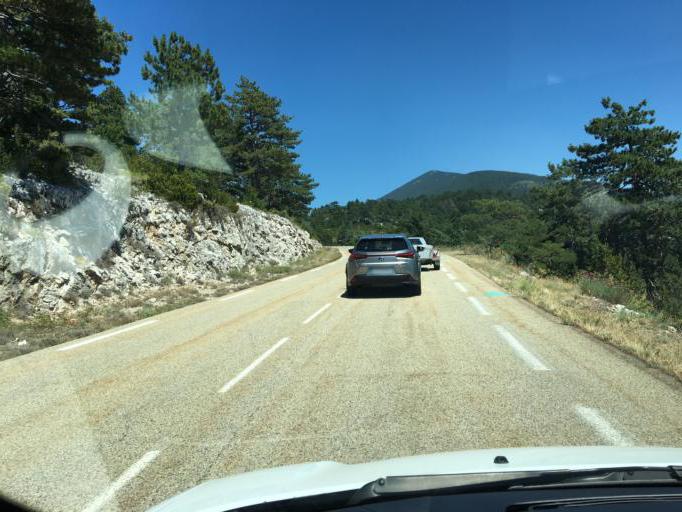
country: FR
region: Provence-Alpes-Cote d'Azur
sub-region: Departement du Vaucluse
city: Bedoin
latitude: 44.1679
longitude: 5.1839
